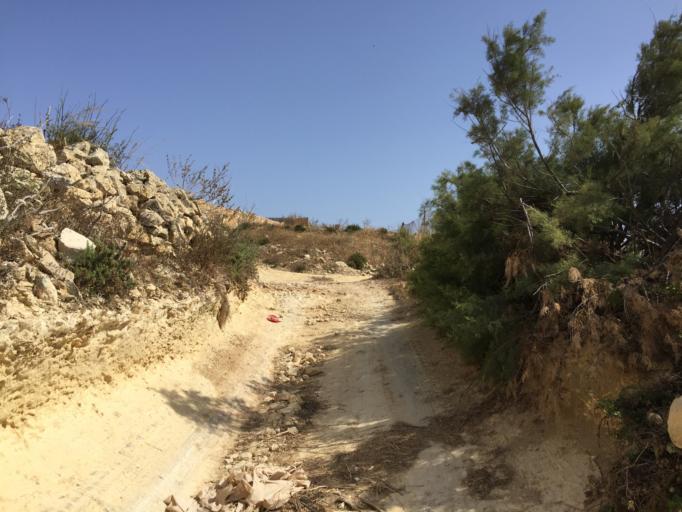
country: MT
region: L-Gharb
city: Gharb
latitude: 36.0722
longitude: 14.2008
